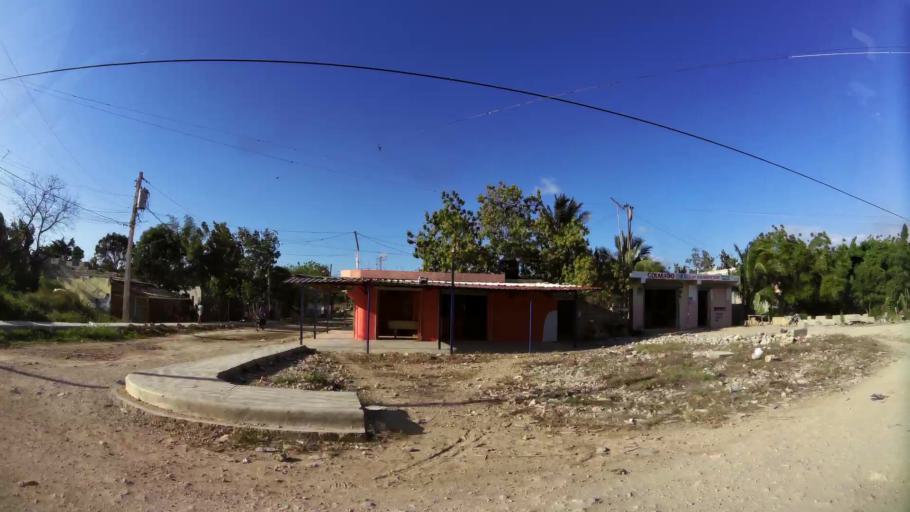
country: DO
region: Santo Domingo
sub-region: Santo Domingo
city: Santo Domingo Este
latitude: 18.4765
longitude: -69.8147
